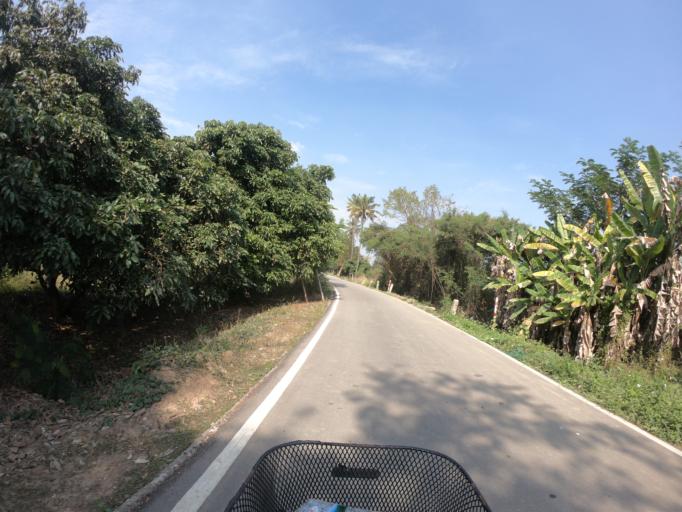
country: TH
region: Chiang Mai
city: Saraphi
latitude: 18.6991
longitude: 99.0571
